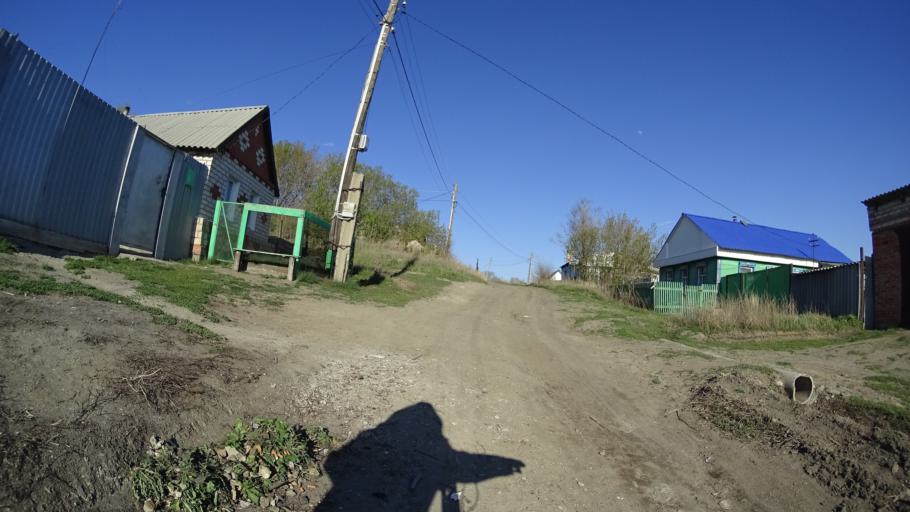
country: RU
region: Chelyabinsk
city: Troitsk
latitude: 54.0985
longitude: 61.5527
